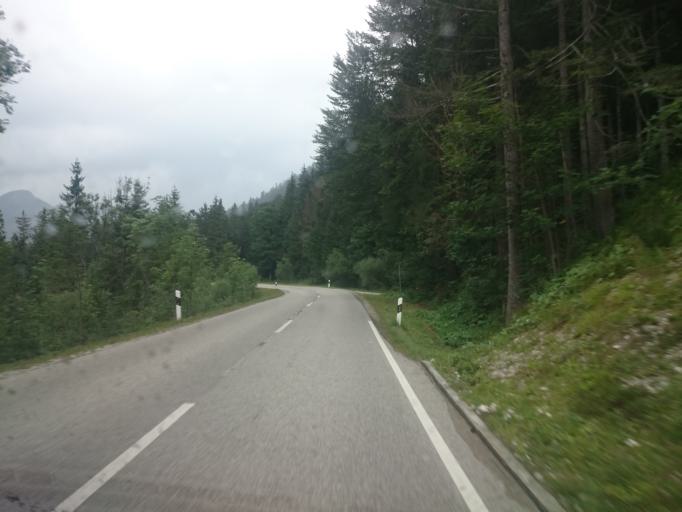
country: DE
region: Bavaria
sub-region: Upper Bavaria
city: Jachenau
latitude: 47.5328
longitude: 11.4411
